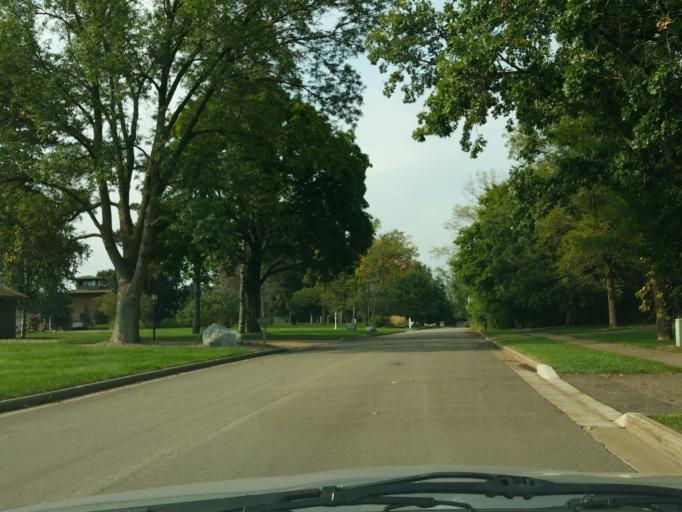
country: US
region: Wisconsin
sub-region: Saint Croix County
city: Hudson
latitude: 44.9599
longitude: -92.7464
